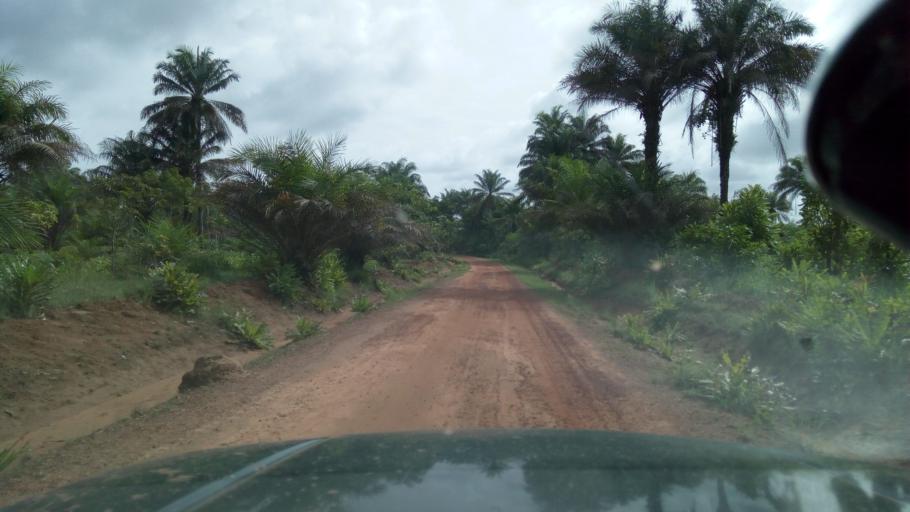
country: SL
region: Northern Province
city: Port Loko
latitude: 8.7919
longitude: -12.9244
